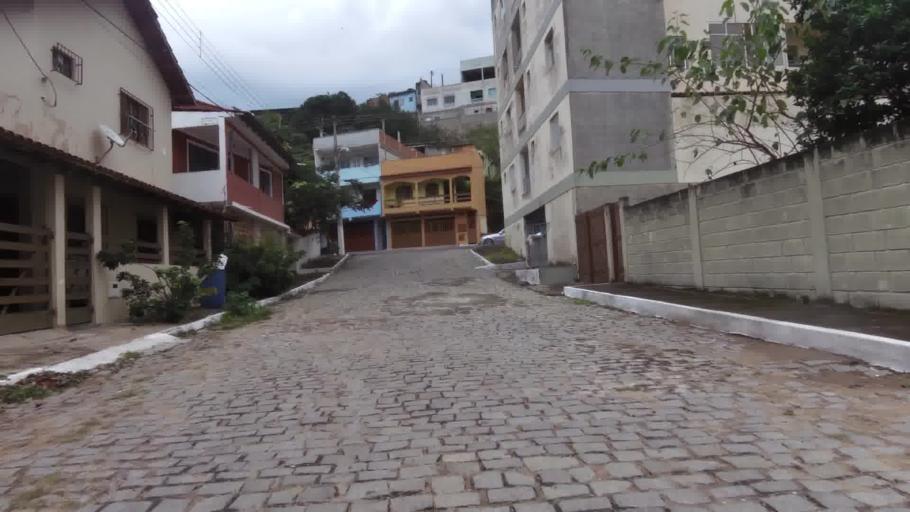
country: BR
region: Espirito Santo
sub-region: Marataizes
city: Marataizes
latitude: -21.0486
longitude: -40.8327
